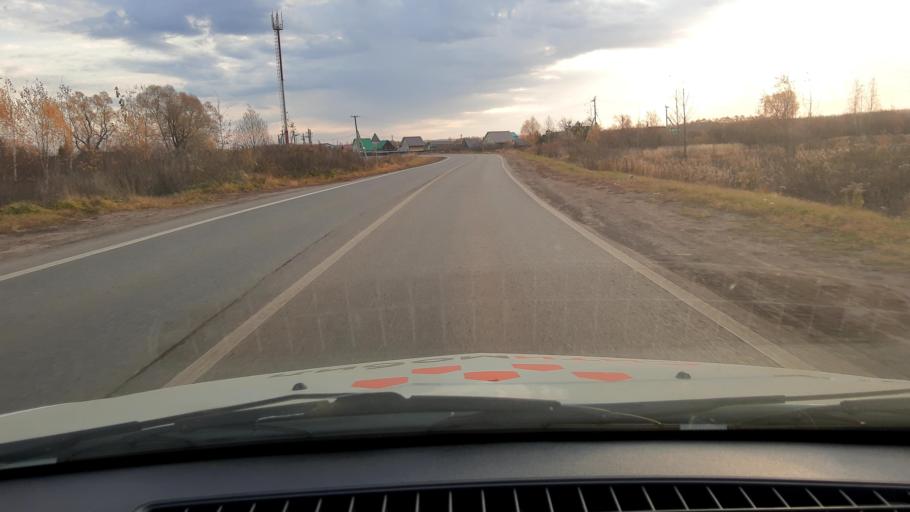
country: RU
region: Bashkortostan
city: Kabakovo
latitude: 54.7220
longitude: 56.1769
